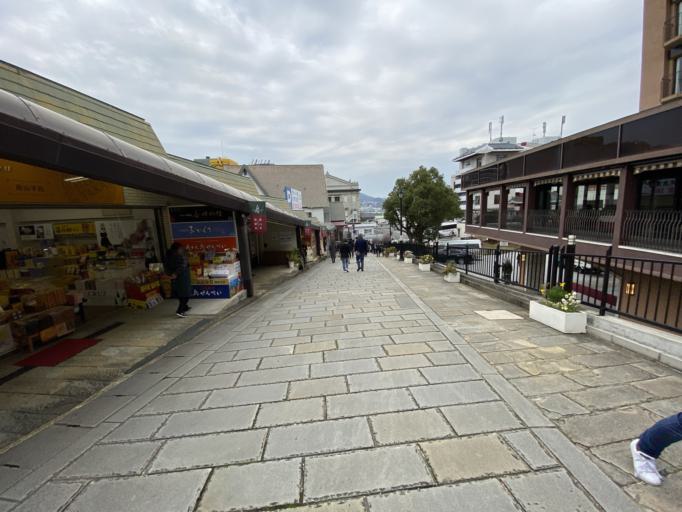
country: JP
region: Nagasaki
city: Nagasaki-shi
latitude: 32.7356
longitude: 129.8698
